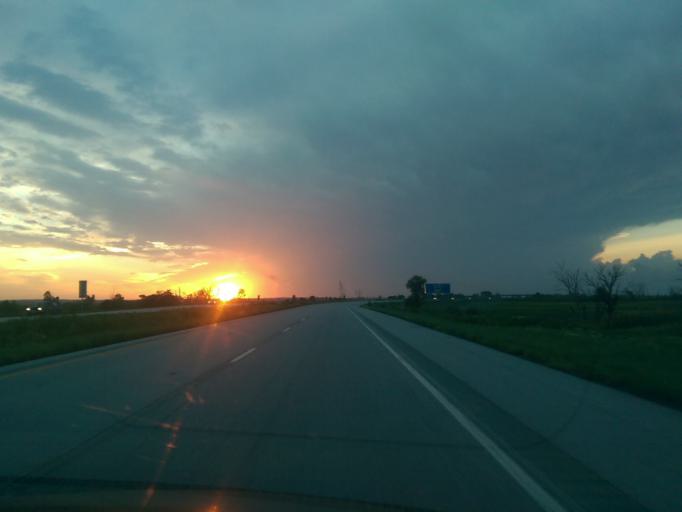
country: US
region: Iowa
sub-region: Fremont County
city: Hamburg
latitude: 40.5926
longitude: -95.6683
